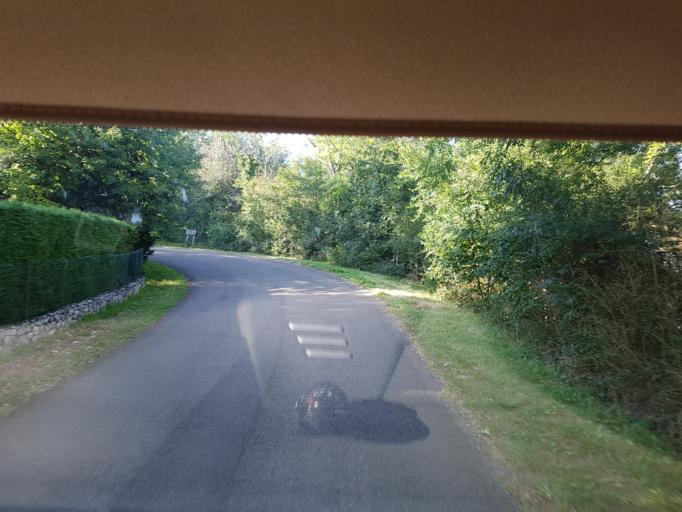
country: FR
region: Rhone-Alpes
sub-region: Departement de l'Ain
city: Poncin
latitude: 46.1387
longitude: 5.4273
